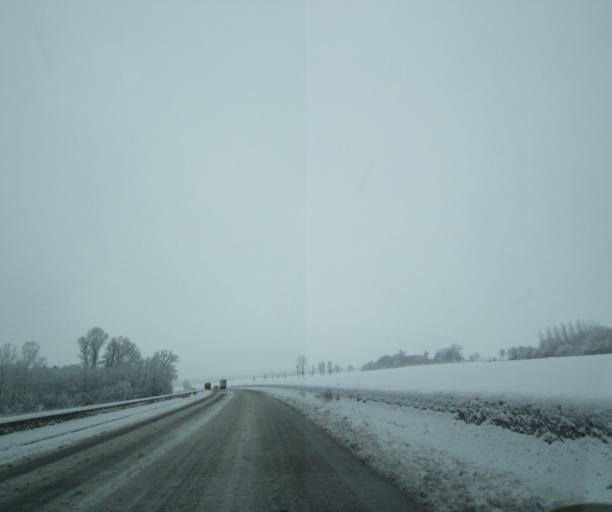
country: FR
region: Champagne-Ardenne
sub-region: Departement de la Haute-Marne
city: Saint-Dizier
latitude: 48.6017
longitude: 4.8995
